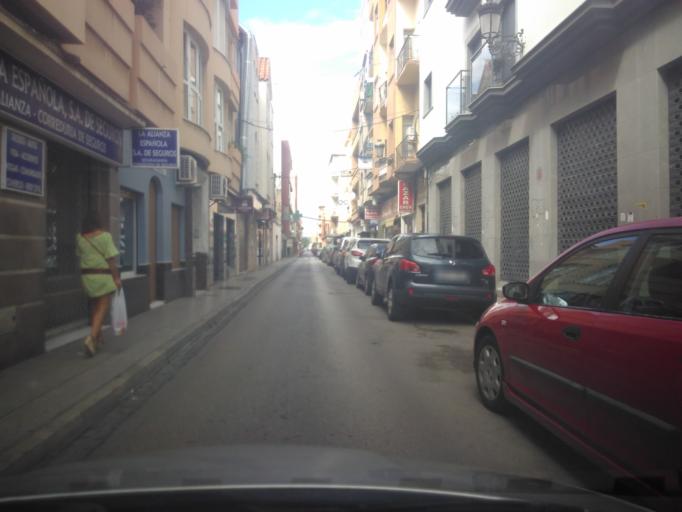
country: ES
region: Andalusia
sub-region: Provincia de Cadiz
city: La Linea de la Concepcion
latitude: 36.1622
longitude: -5.3482
